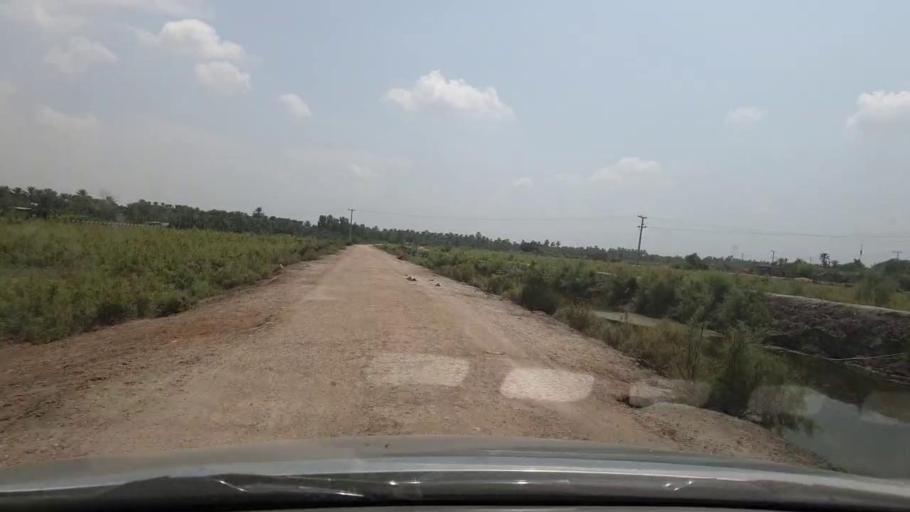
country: PK
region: Sindh
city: Kot Diji
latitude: 27.3779
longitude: 68.7109
